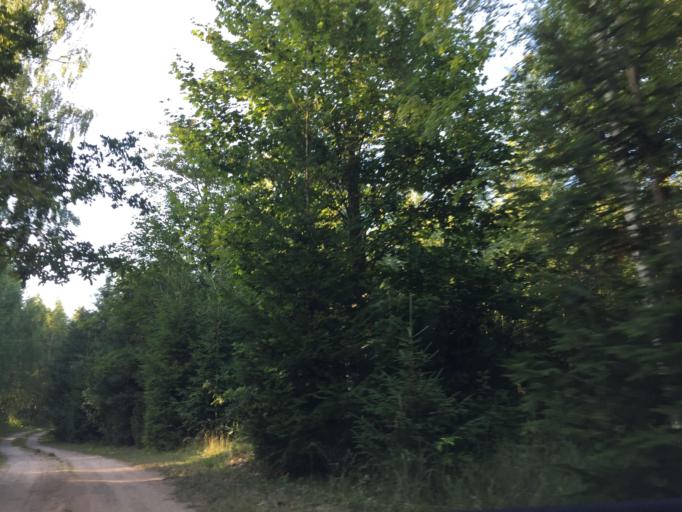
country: LV
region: Talsu Rajons
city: Stende
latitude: 57.1605
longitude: 22.3039
